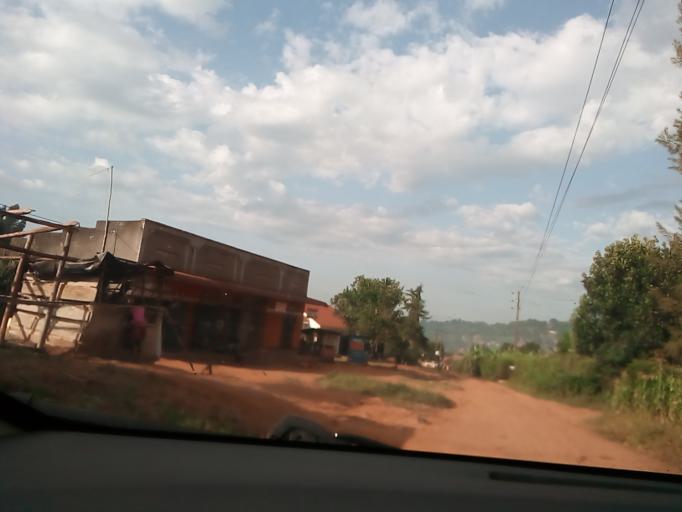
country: UG
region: Central Region
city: Masaka
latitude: -0.3454
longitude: 31.7254
